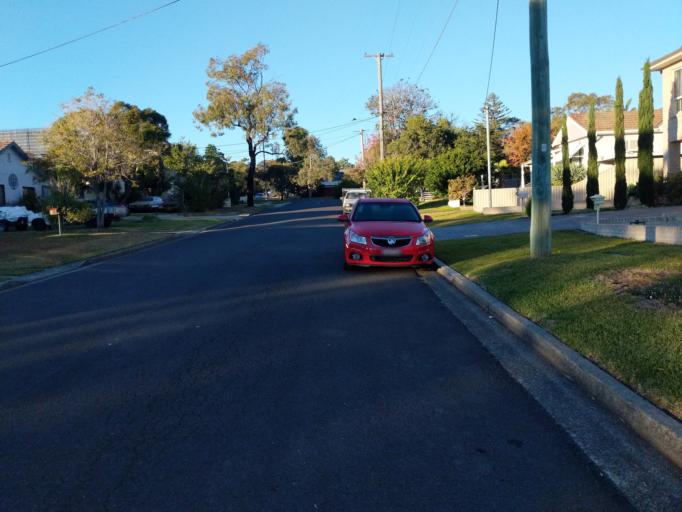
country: AU
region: New South Wales
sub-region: Sutherland Shire
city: Kirrawee
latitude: -34.0290
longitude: 151.0704
